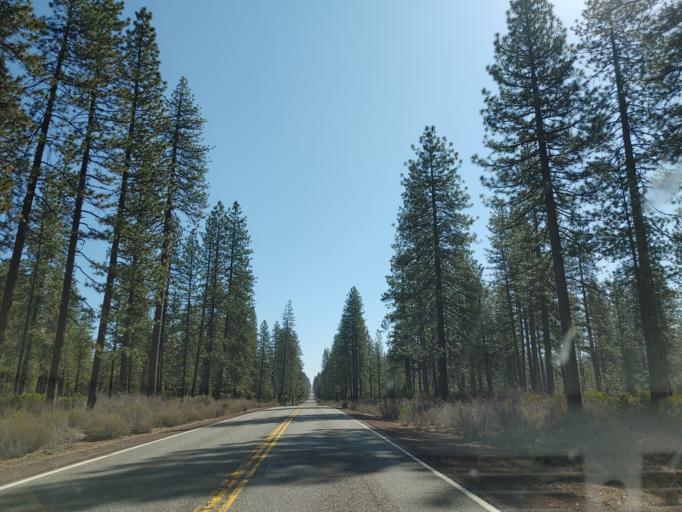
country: US
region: California
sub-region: Siskiyou County
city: McCloud
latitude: 41.2564
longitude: -122.0364
